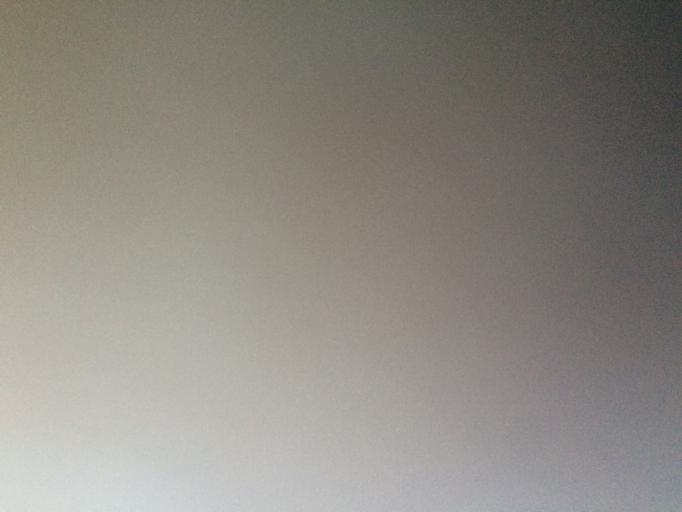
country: SE
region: Norrbotten
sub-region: Lulea Kommun
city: Gammelstad
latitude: 65.6873
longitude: 22.1088
